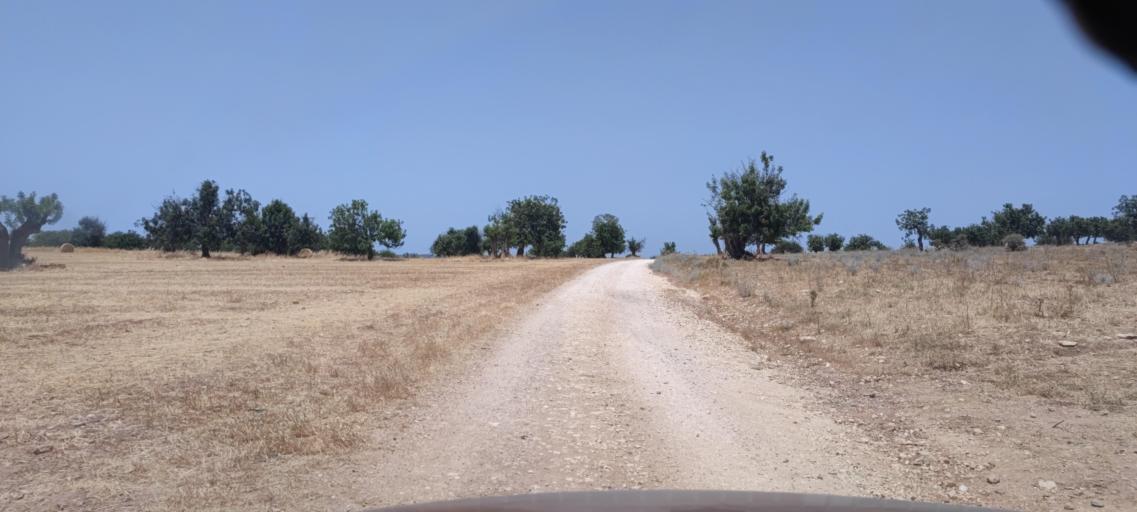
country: CY
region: Limassol
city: Pissouri
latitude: 34.7236
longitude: 32.5931
